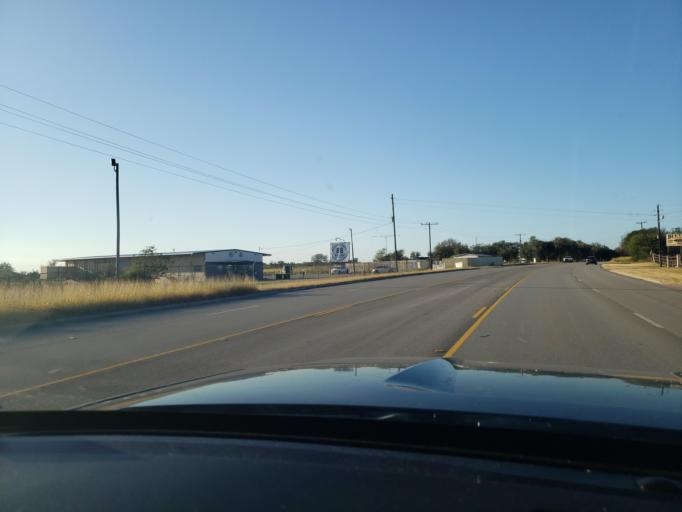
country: US
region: Texas
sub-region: Bee County
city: Beeville
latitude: 28.4214
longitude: -97.7180
